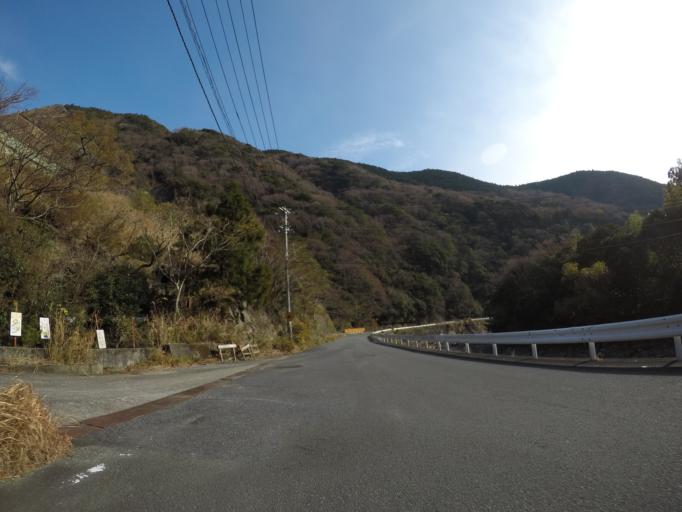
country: JP
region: Shizuoka
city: Heda
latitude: 34.7994
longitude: 138.8075
